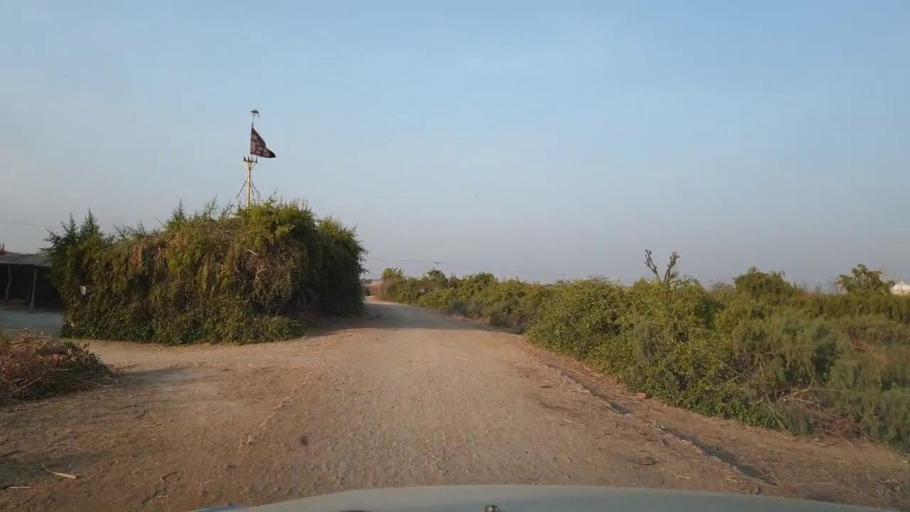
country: PK
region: Sindh
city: Pithoro
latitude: 25.6572
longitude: 69.2134
